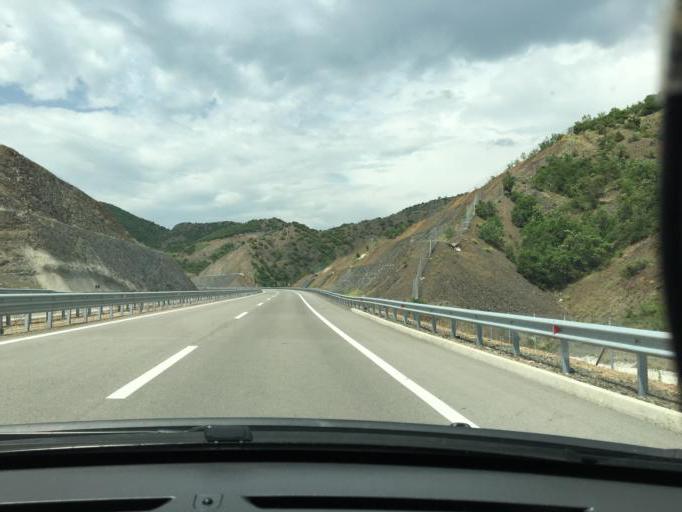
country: MK
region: Demir Kapija
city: Demir Kapija
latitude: 41.3717
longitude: 22.3312
